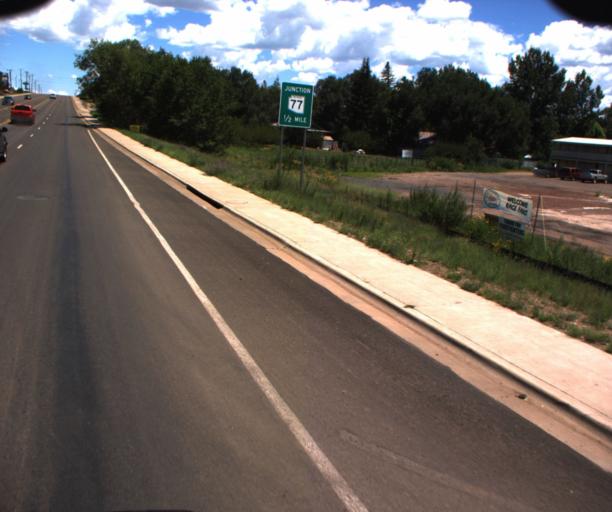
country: US
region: Arizona
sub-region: Navajo County
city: Show Low
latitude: 34.2549
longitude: -110.0264
